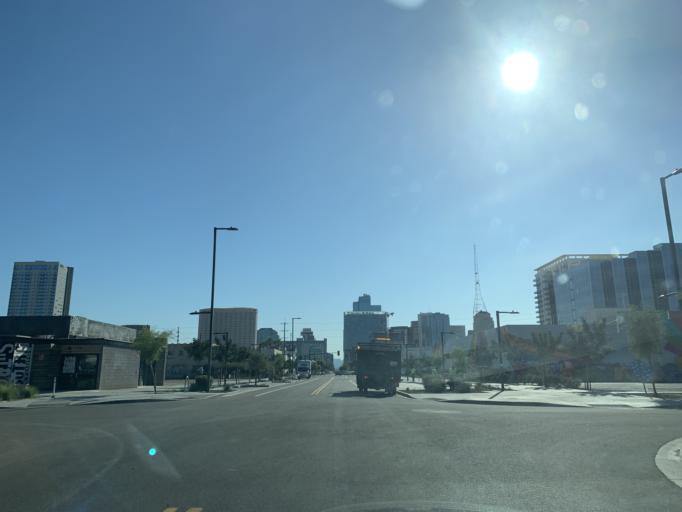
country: US
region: Arizona
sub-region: Maricopa County
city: Phoenix
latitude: 33.4602
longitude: -112.0726
